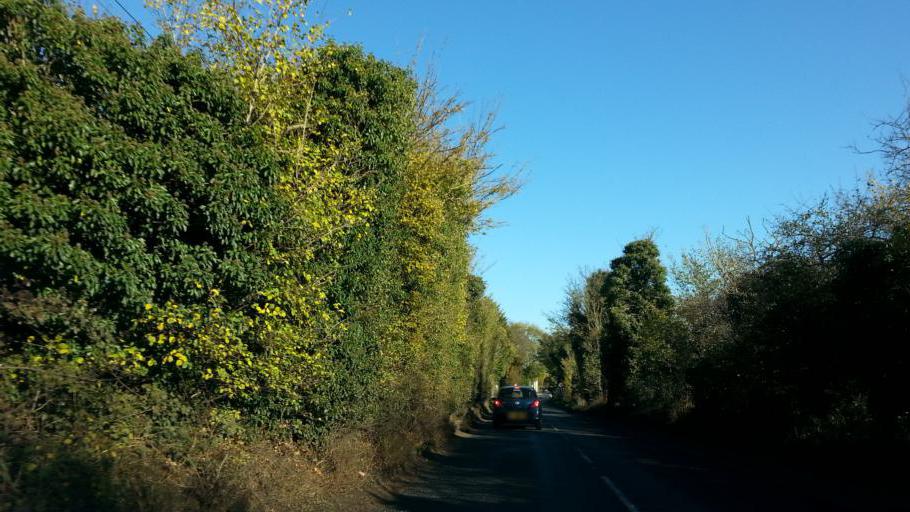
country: GB
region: England
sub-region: Suffolk
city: Wickham Market
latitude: 52.1135
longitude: 1.3791
